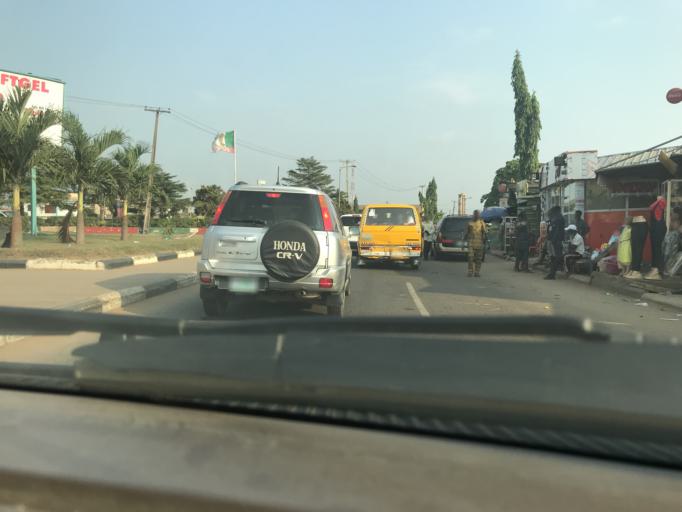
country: NG
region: Lagos
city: Ikotun
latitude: 6.5764
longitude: 3.2805
